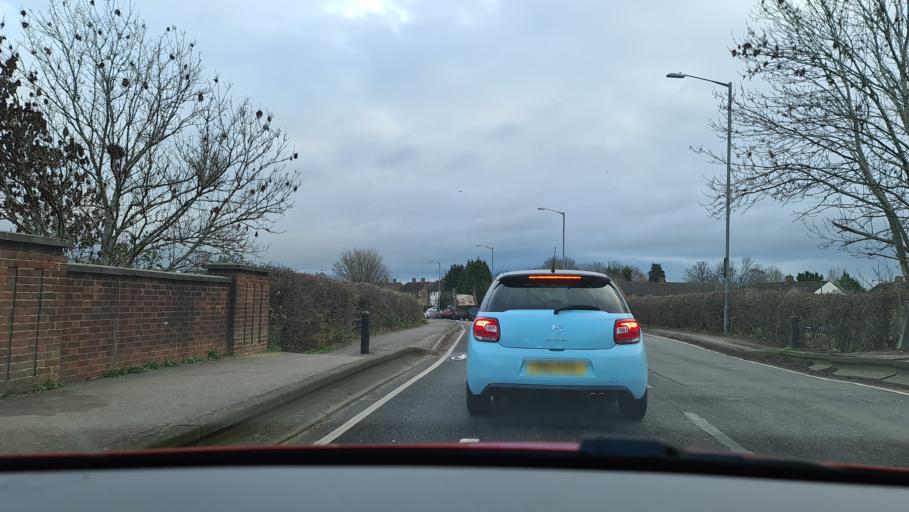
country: GB
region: England
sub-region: Buckinghamshire
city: Aylesbury
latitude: 51.7987
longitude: -0.8102
